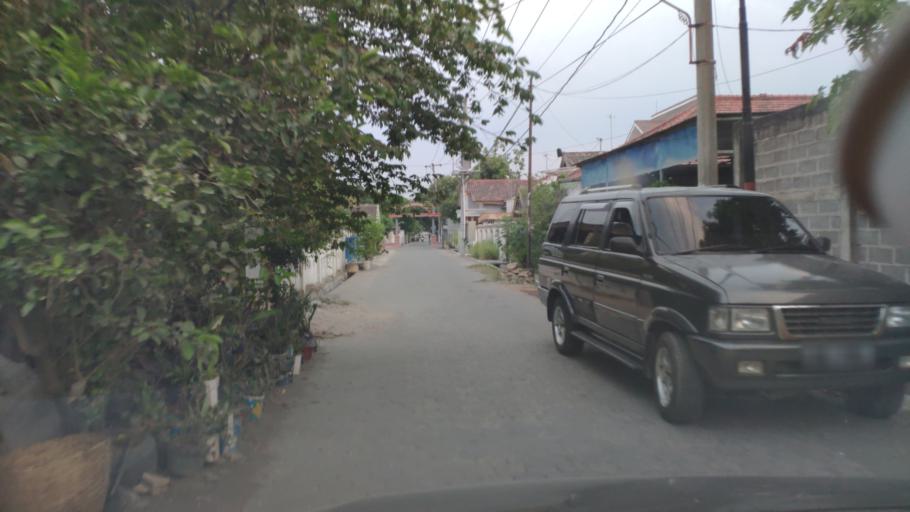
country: ID
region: Central Java
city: Cepu
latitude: -7.1521
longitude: 111.5851
